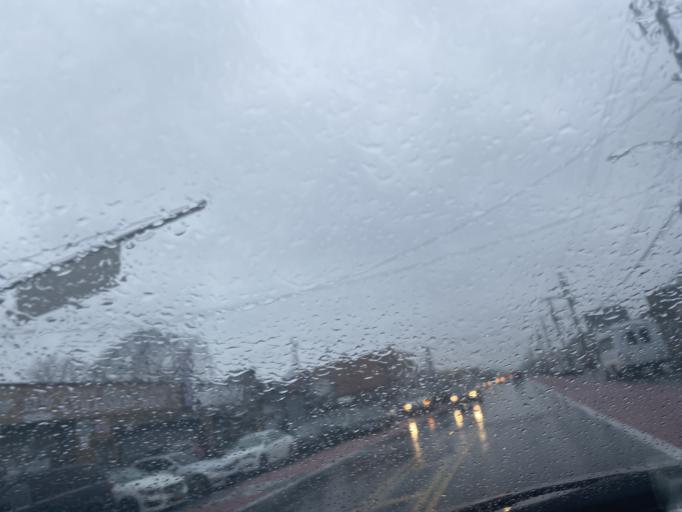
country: US
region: New York
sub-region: Kings County
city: Brooklyn
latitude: 40.6425
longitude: -73.9293
